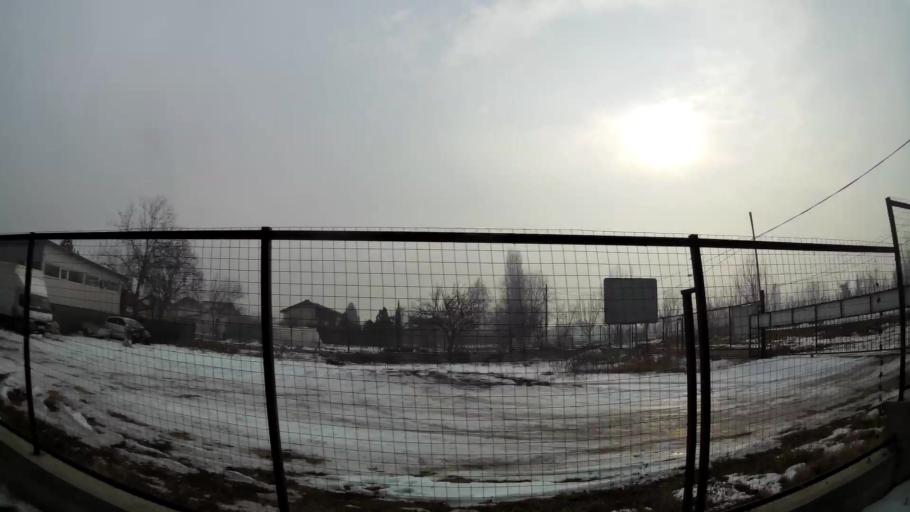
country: MK
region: Ilinden
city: Jurumleri
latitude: 41.9742
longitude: 21.5386
